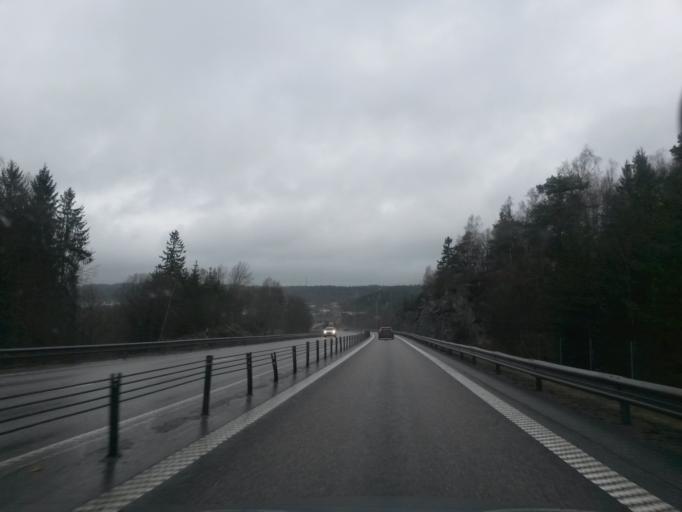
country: SE
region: Vaestra Goetaland
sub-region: Uddevalla Kommun
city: Uddevalla
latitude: 58.3448
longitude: 11.9883
